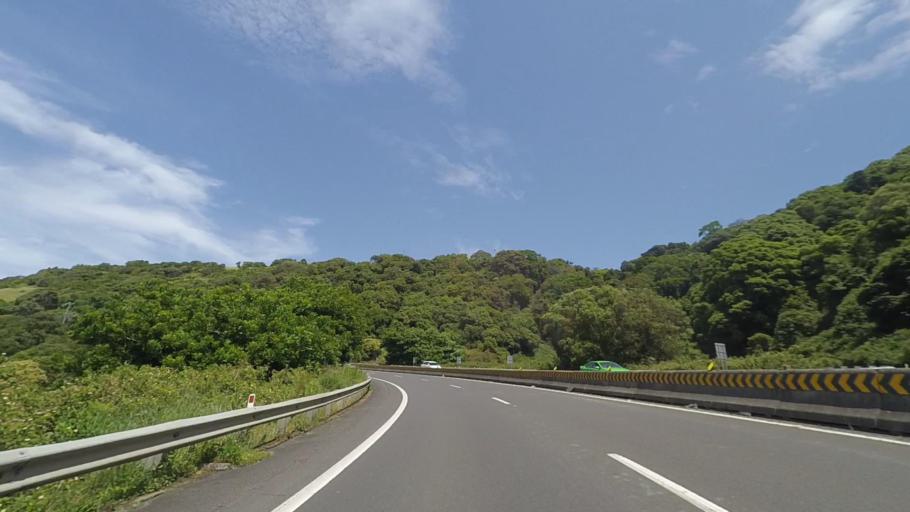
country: AU
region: New South Wales
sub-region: Kiama
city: Kiama
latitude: -34.7016
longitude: 150.8367
